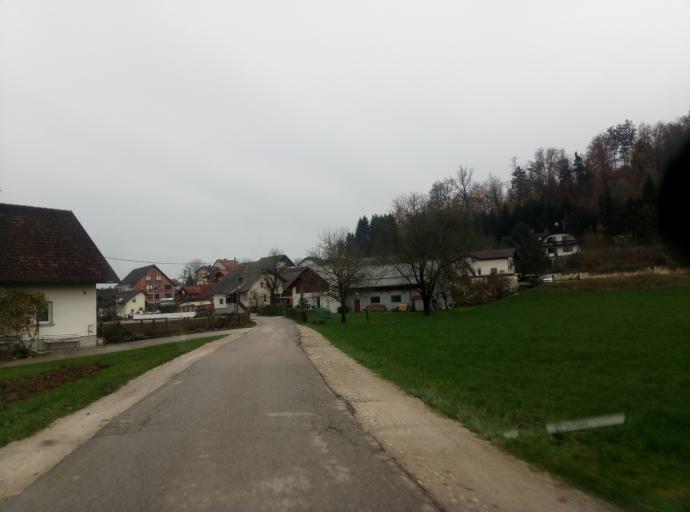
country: SI
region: Vodice
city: Vodice
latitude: 46.1783
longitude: 14.4813
